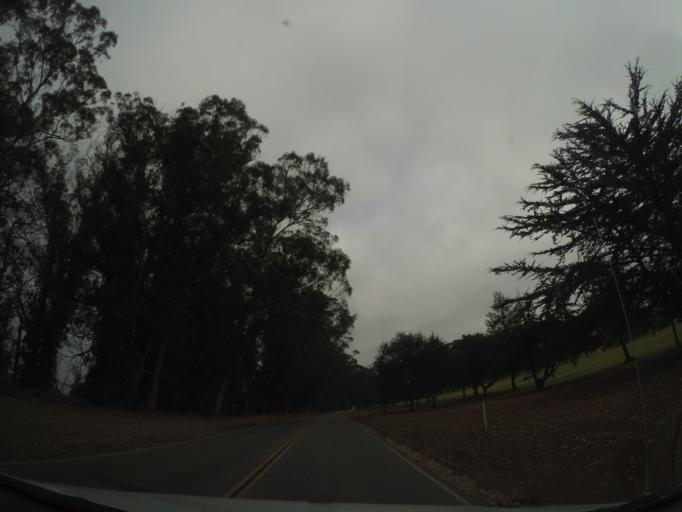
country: US
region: California
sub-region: San Luis Obispo County
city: Morro Bay
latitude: 35.3513
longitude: -120.8433
